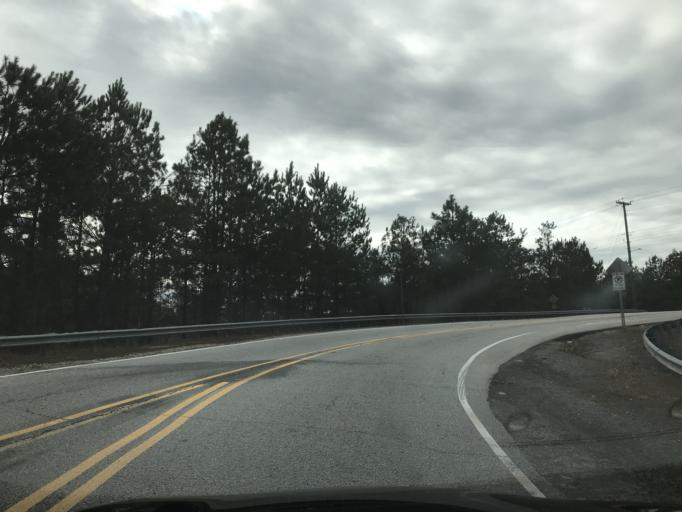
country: US
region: Georgia
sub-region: Carroll County
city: Villa Rica
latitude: 33.7279
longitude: -84.8991
